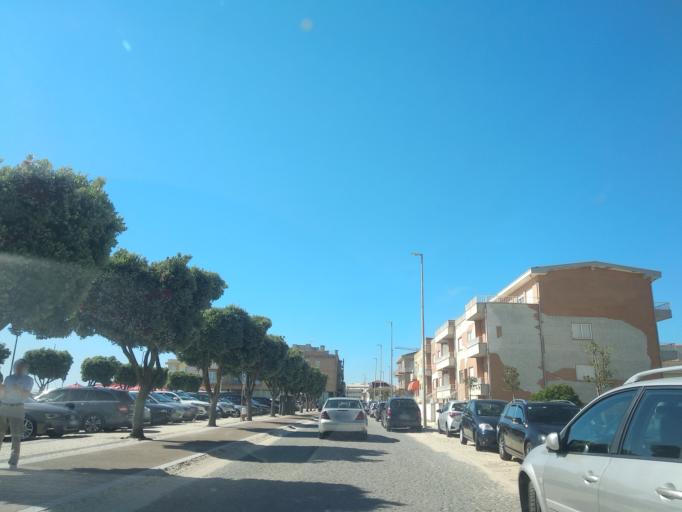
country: PT
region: Braga
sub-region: Esposende
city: Apulia
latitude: 41.4829
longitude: -8.7763
